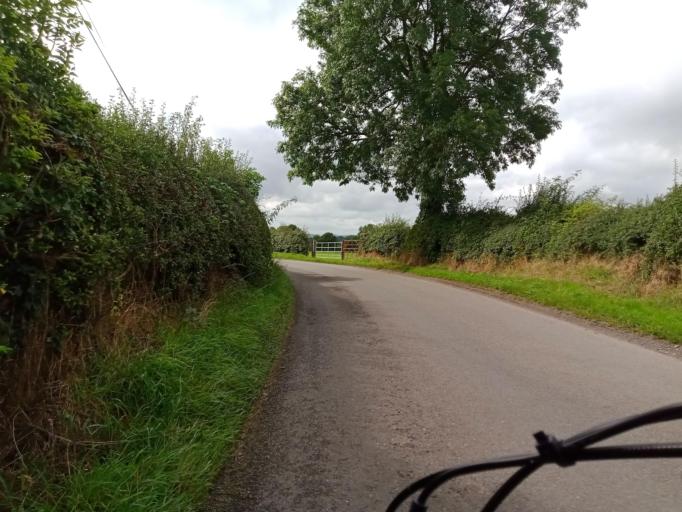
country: IE
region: Leinster
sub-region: Kilkenny
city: Callan
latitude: 52.5314
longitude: -7.2835
